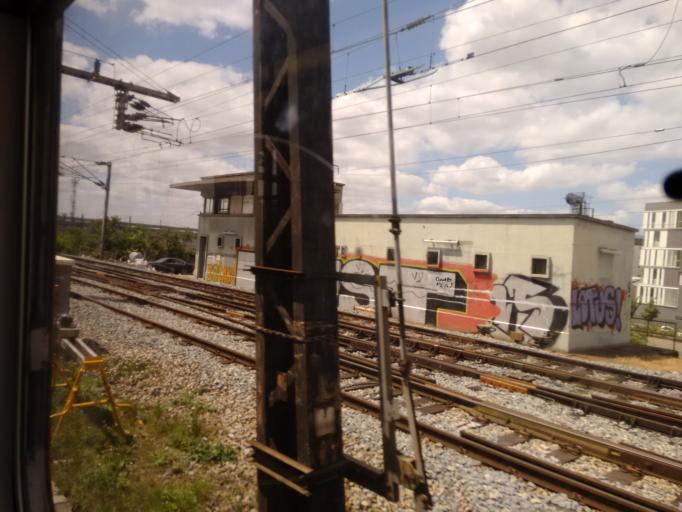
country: FR
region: Ile-de-France
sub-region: Departement de Seine-Saint-Denis
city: Saint-Denis
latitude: 48.9140
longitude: 2.3551
